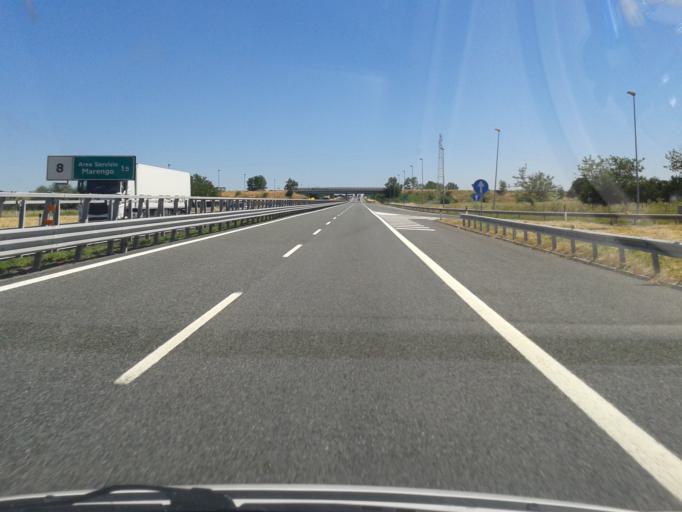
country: IT
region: Piedmont
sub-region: Provincia di Alessandria
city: Basaluzzo
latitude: 44.7905
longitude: 8.7328
